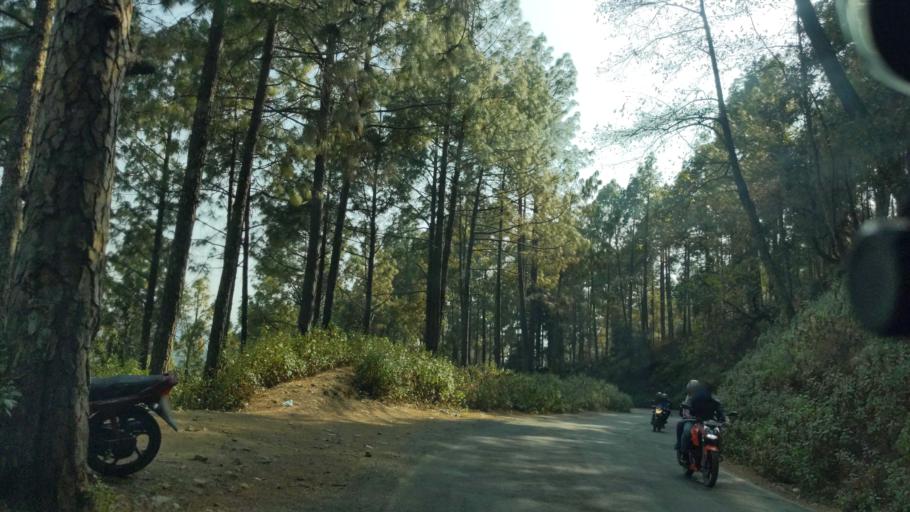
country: IN
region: Uttarakhand
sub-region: Naini Tal
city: Bhowali
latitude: 29.4005
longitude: 79.5383
